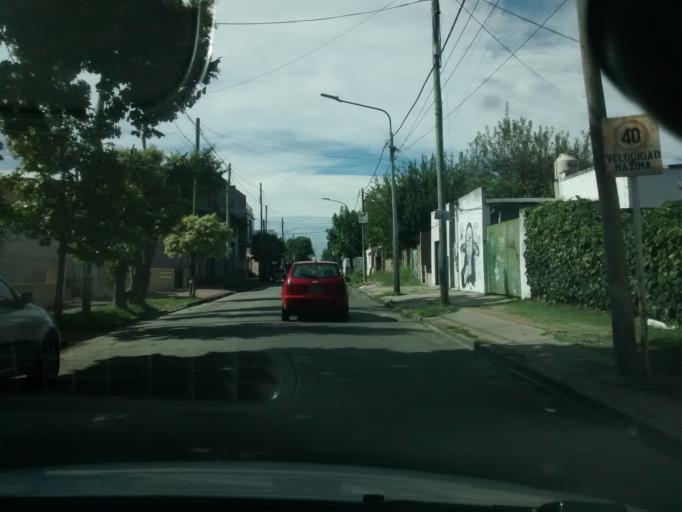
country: AR
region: Buenos Aires
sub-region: Partido de Moron
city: Moron
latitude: -34.6614
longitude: -58.6223
